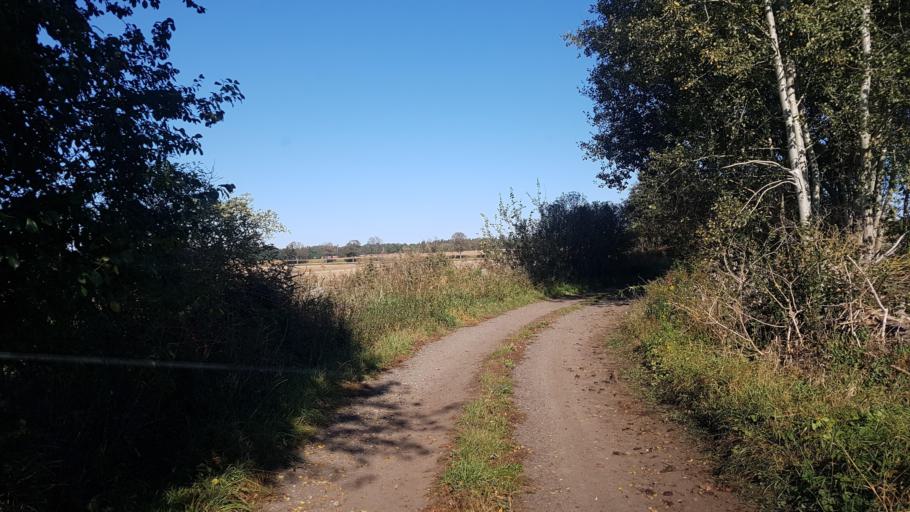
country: DE
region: Brandenburg
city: Plessa
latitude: 51.4651
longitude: 13.5870
